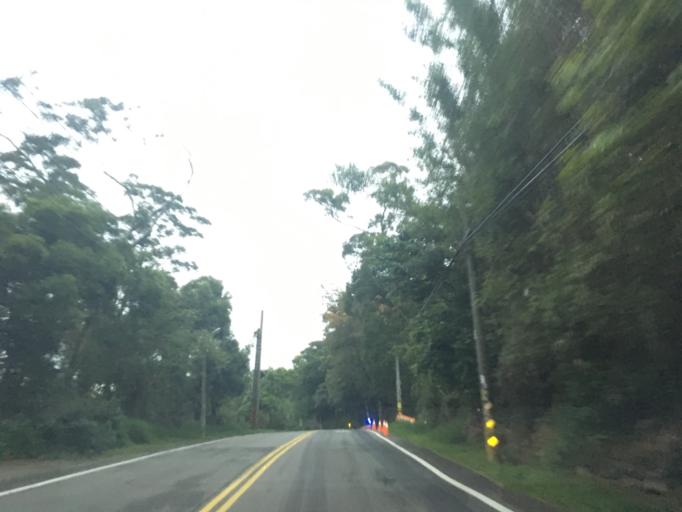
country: TW
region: Taiwan
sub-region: Miaoli
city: Miaoli
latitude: 24.4501
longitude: 120.7801
